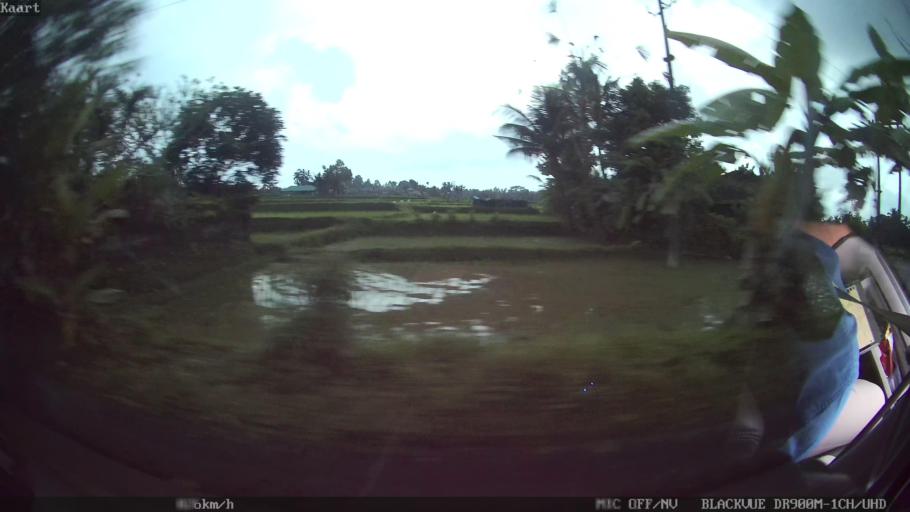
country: ID
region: Bali
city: Bayad
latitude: -8.4519
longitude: 115.2429
